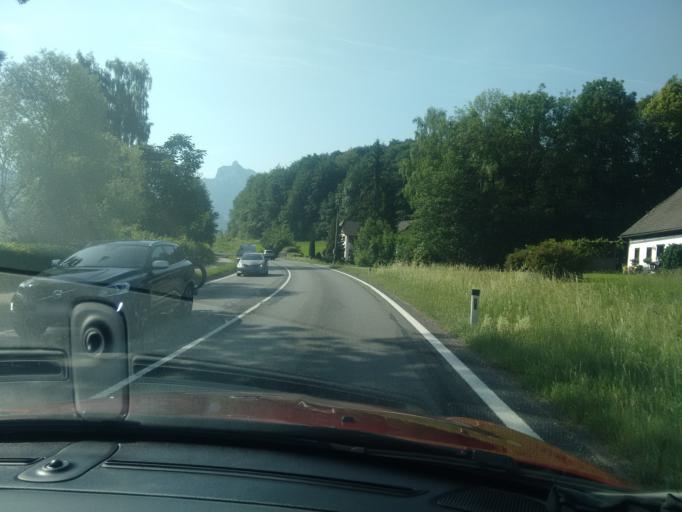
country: AT
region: Upper Austria
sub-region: Politischer Bezirk Gmunden
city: Altmunster
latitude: 47.8736
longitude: 13.7760
